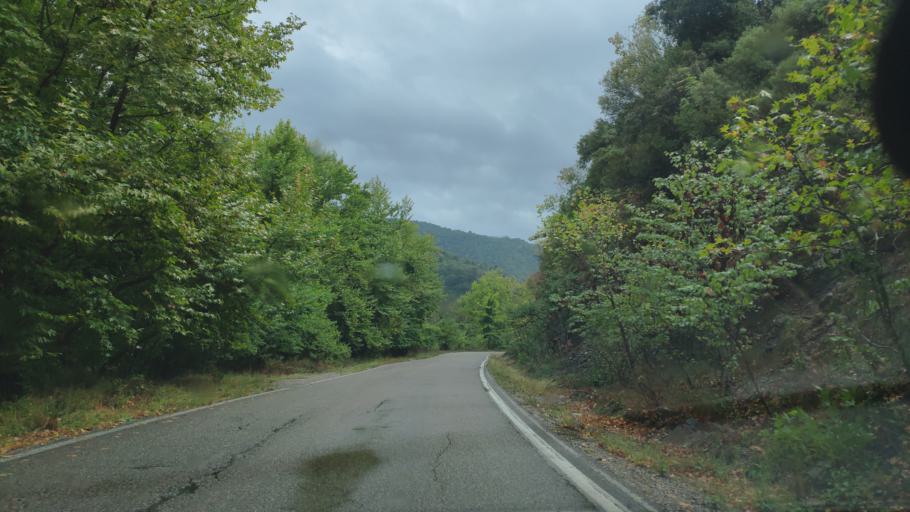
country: GR
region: West Greece
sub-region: Nomos Aitolias kai Akarnanias
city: Krikellos
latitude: 38.9590
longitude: 21.3362
